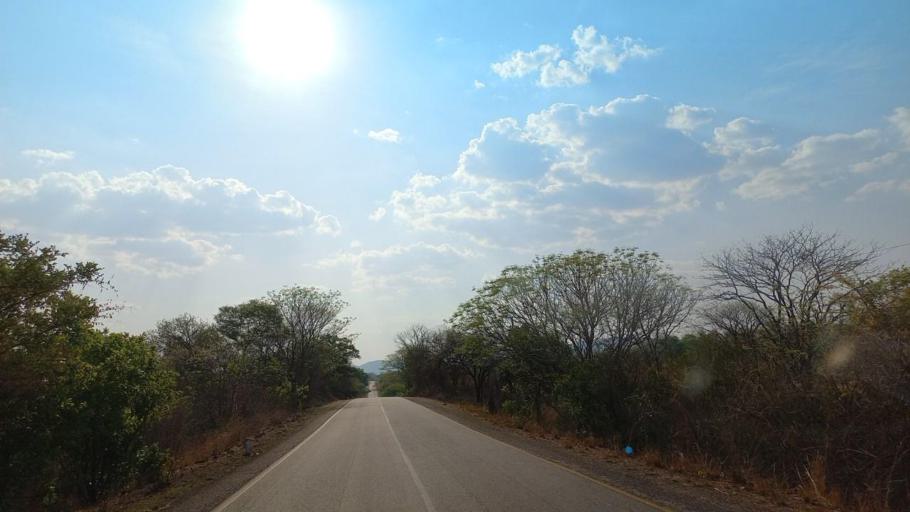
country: ZM
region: Lusaka
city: Luangwa
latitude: -14.9824
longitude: 30.1348
